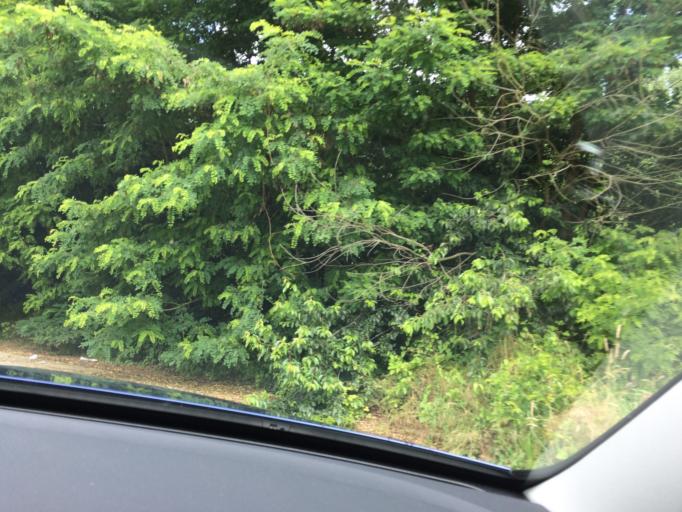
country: BE
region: Flanders
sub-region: Provincie Vlaams-Brabant
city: Oud-Heverlee
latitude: 50.8647
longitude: 4.6643
